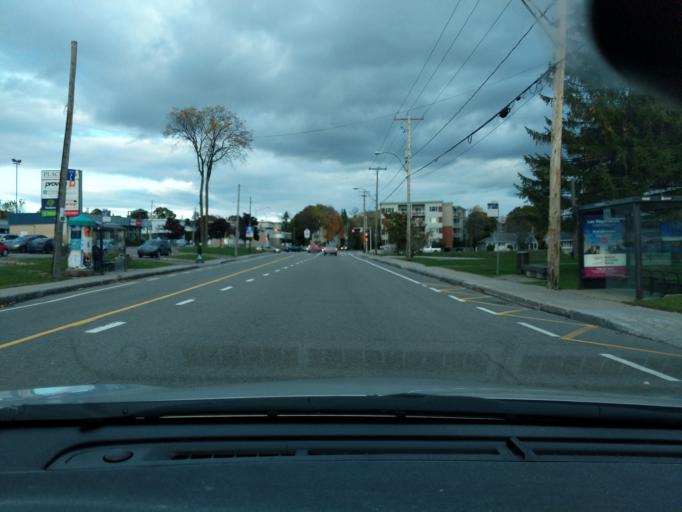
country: CA
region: Quebec
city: L'Ancienne-Lorette
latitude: 46.7618
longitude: -71.2835
